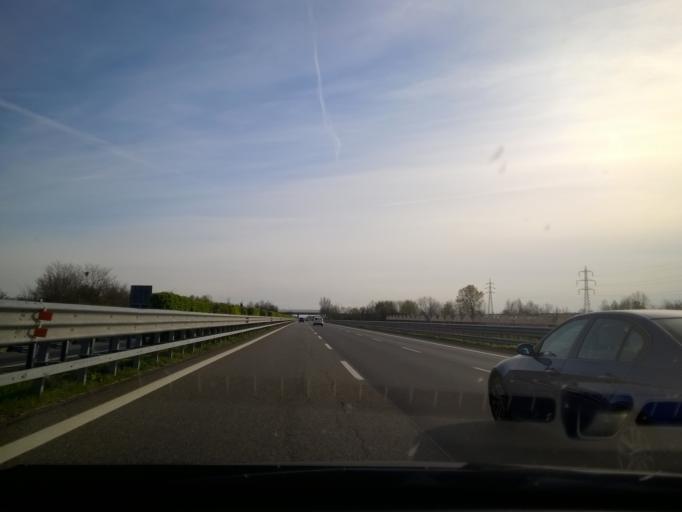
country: IT
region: Lombardy
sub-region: Provincia di Brescia
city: Montirone
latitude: 45.4577
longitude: 10.2154
